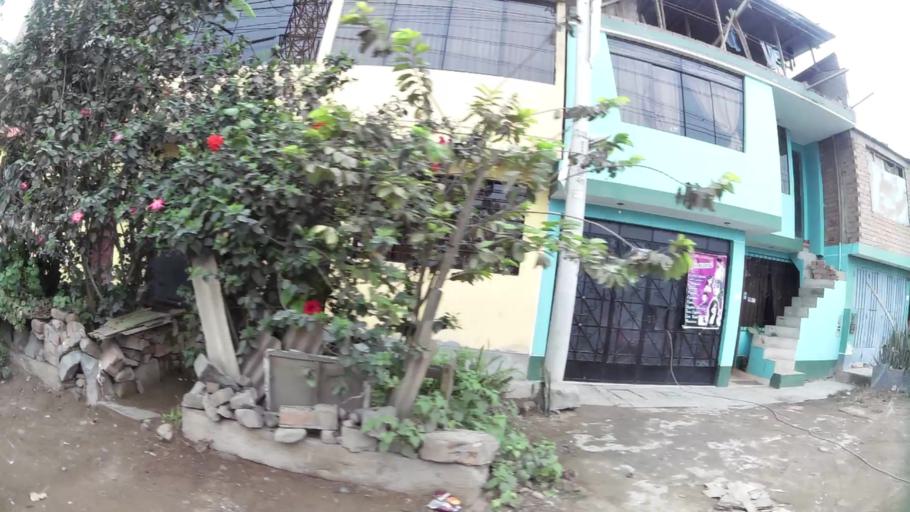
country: PE
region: Lima
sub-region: Lima
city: Surco
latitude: -12.1901
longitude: -76.9373
